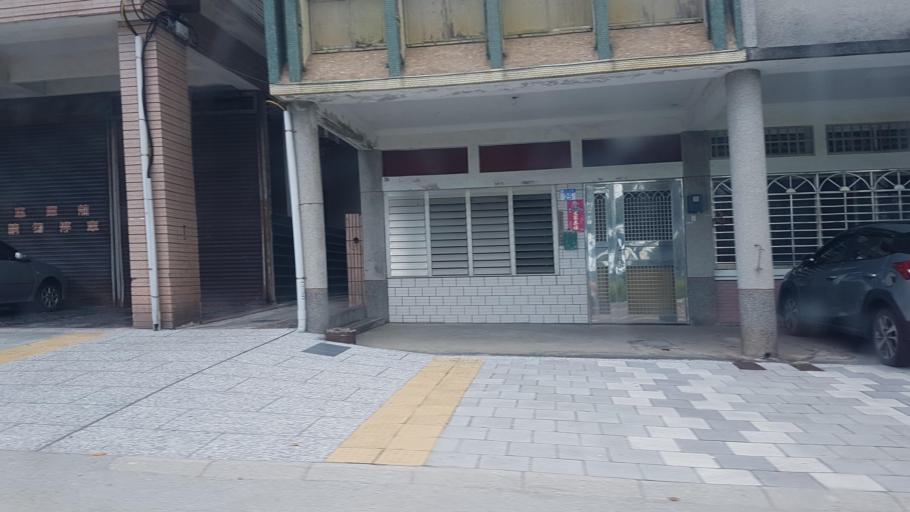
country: TW
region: Taiwan
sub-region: Hualien
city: Hualian
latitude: 23.9937
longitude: 121.6336
